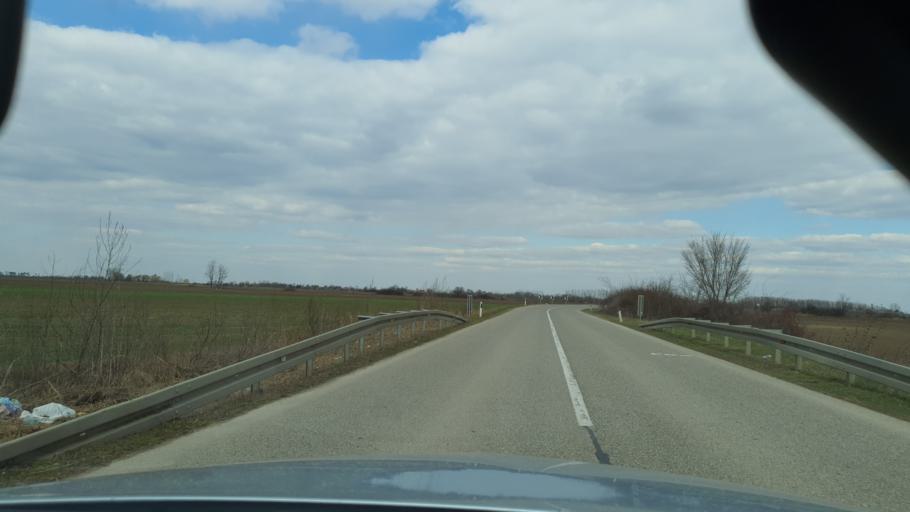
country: RS
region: Autonomna Pokrajina Vojvodina
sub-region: Zapadnobacki Okrug
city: Odzaci
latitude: 45.4411
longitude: 19.3162
